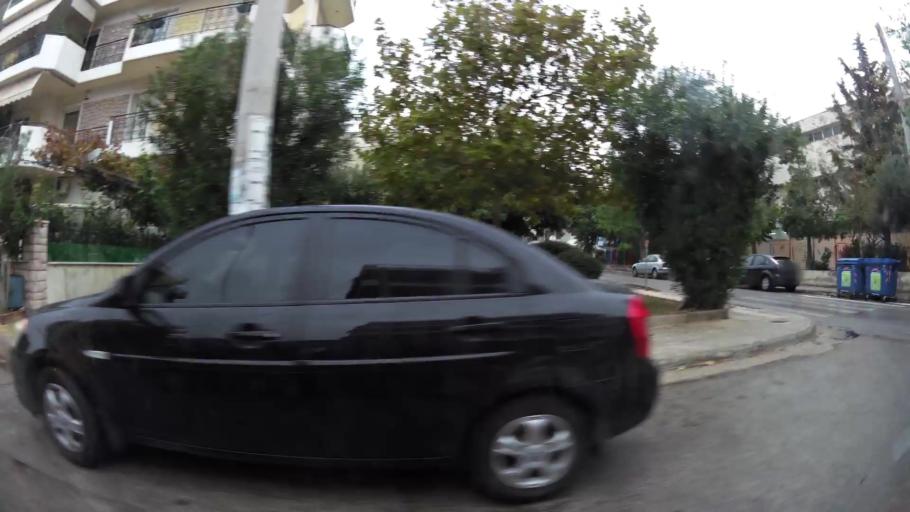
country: GR
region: Attica
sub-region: Nomarchia Athinas
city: Nea Filadelfeia
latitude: 38.0402
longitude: 23.7302
